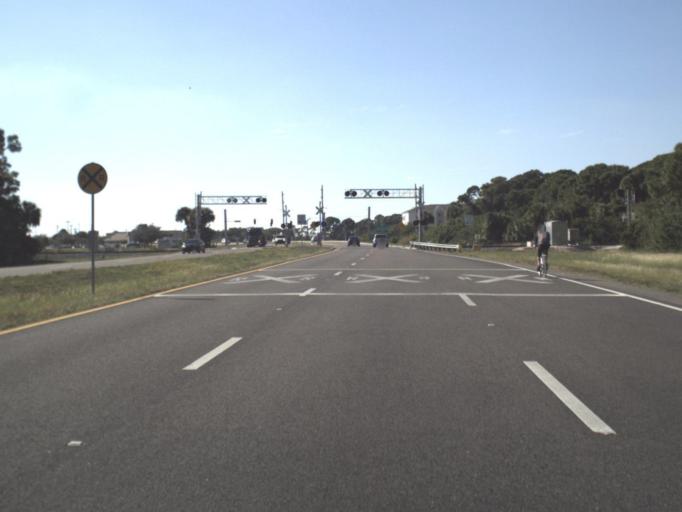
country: US
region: Florida
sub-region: Brevard County
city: South Patrick Shores
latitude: 28.2044
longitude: -80.6653
